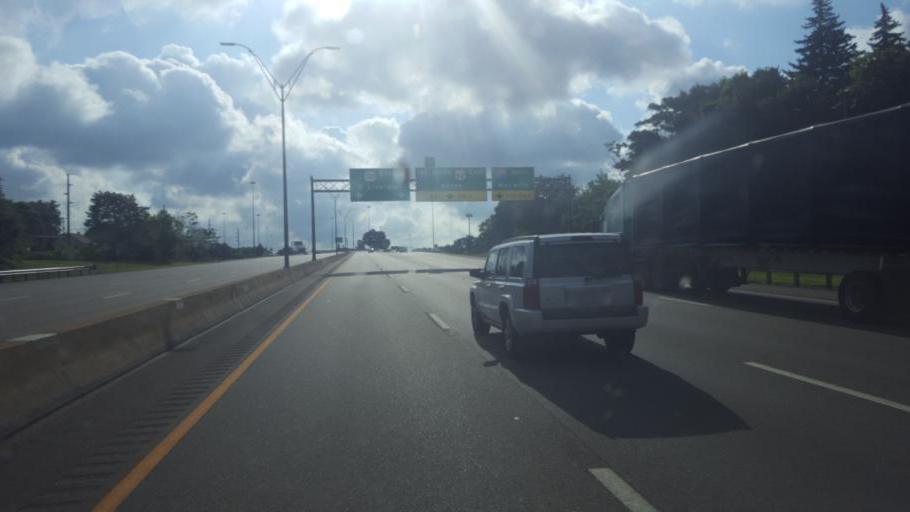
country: US
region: Ohio
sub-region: Stark County
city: Canton
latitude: 40.7845
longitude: -81.3923
